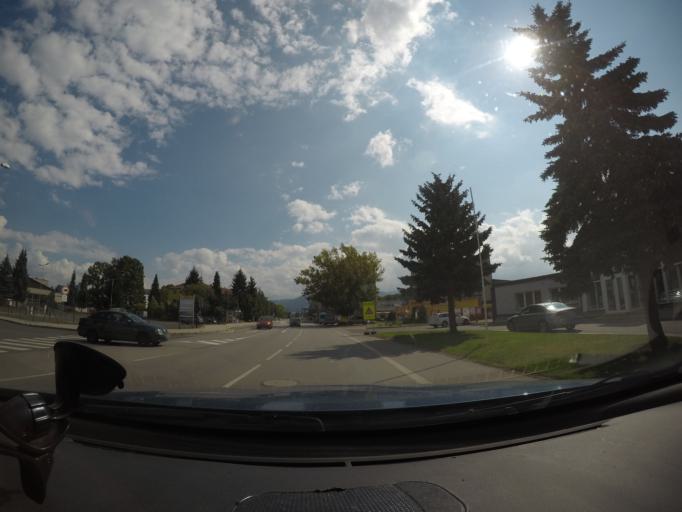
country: SK
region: Zilinsky
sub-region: Okres Liptovsky Mikulas
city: Liptovsky Mikulas
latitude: 49.0882
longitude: 19.6033
